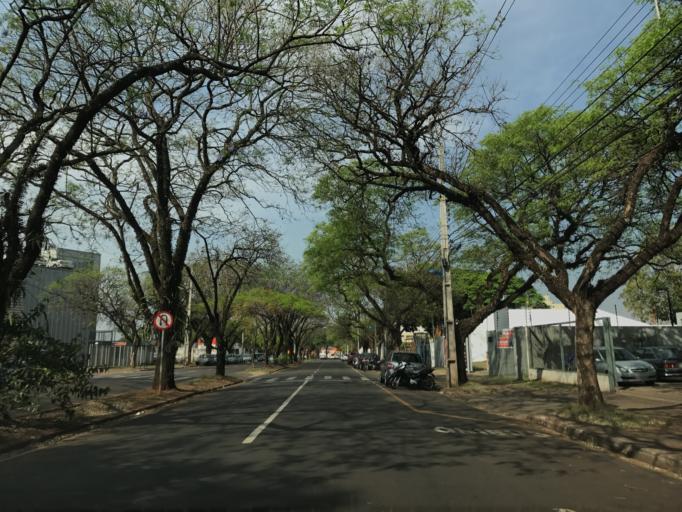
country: BR
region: Parana
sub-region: Maringa
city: Maringa
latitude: -23.4182
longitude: -51.9212
